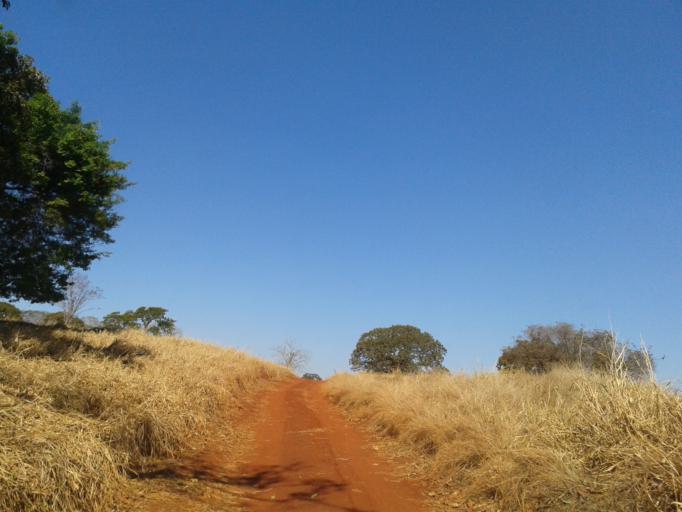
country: BR
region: Minas Gerais
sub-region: Santa Vitoria
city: Santa Vitoria
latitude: -19.1441
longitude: -50.0354
